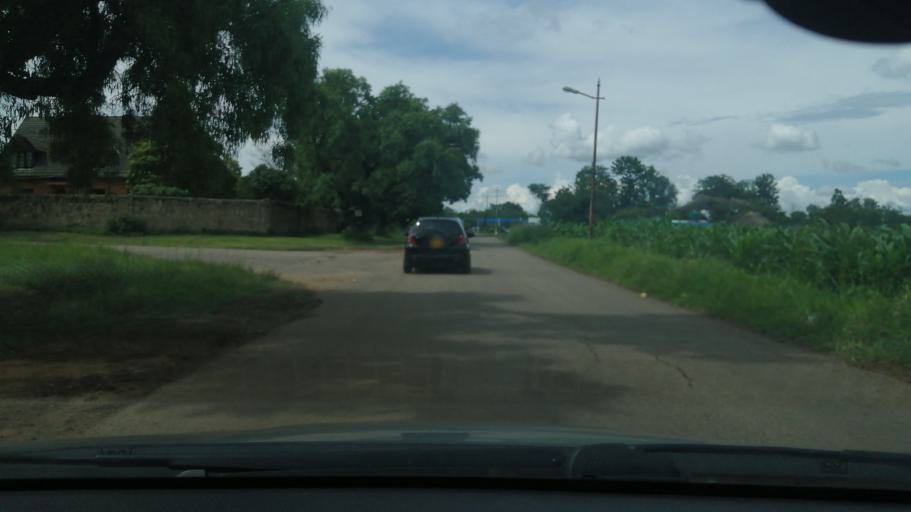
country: ZW
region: Harare
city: Harare
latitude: -17.8160
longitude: 31.0707
